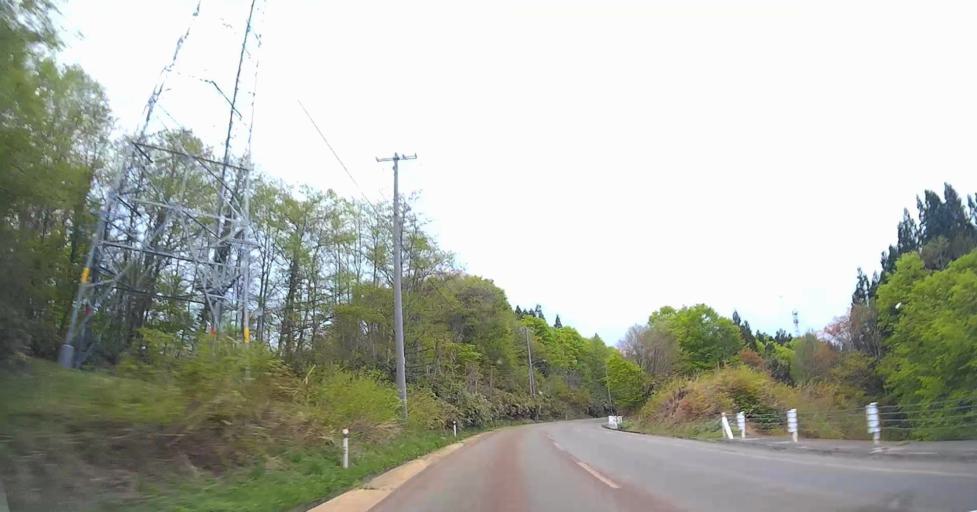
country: JP
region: Aomori
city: Goshogawara
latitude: 41.1080
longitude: 140.5390
